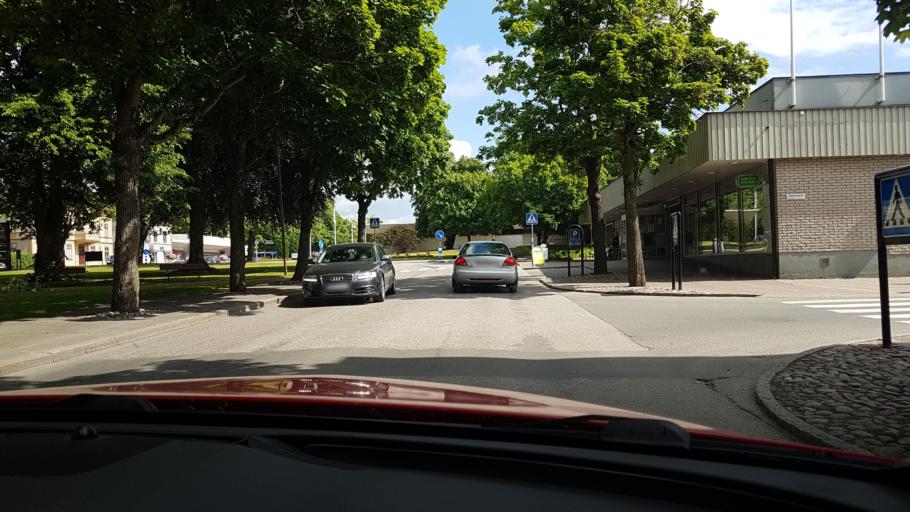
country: SE
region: Vaestra Goetaland
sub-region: Hjo Kommun
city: Hjo
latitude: 58.3030
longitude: 14.2910
